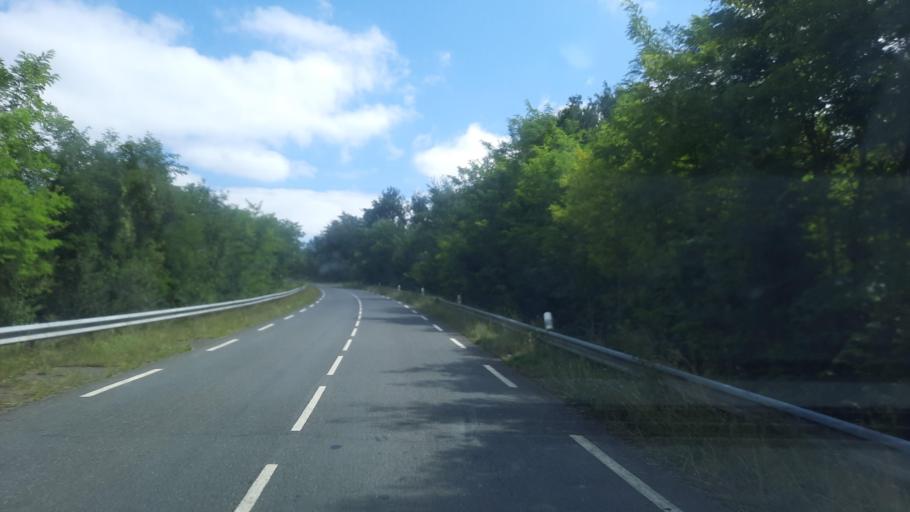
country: FR
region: Midi-Pyrenees
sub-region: Departement de la Haute-Garonne
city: Boulogne-sur-Gesse
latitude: 43.2919
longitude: 0.6312
